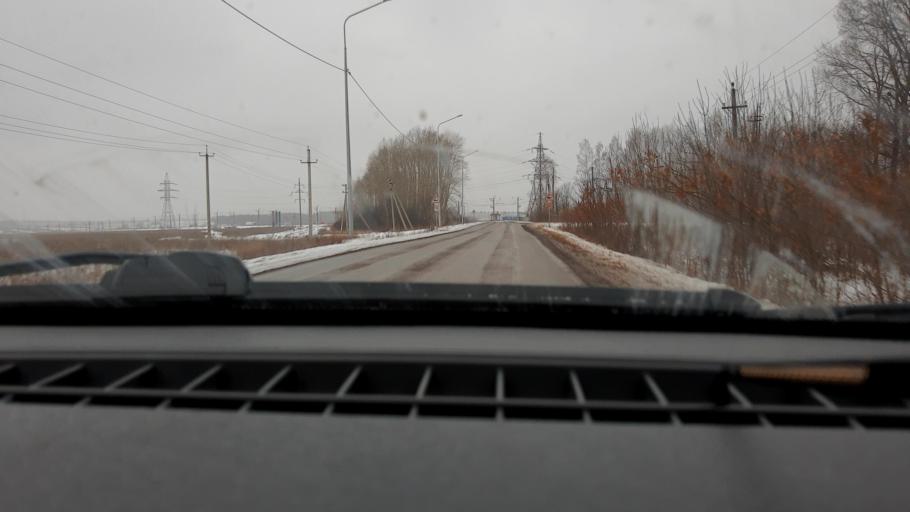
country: RU
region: Bashkortostan
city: Kabakovo
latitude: 54.7010
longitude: 56.2213
